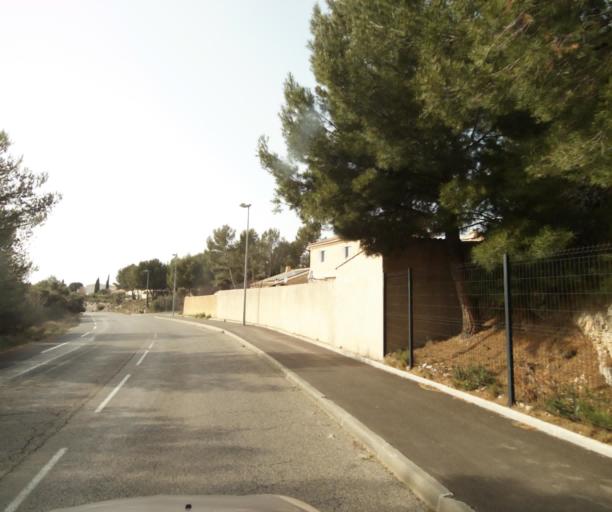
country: FR
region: Provence-Alpes-Cote d'Azur
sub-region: Departement des Bouches-du-Rhone
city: Vitrolles
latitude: 43.4624
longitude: 5.2399
